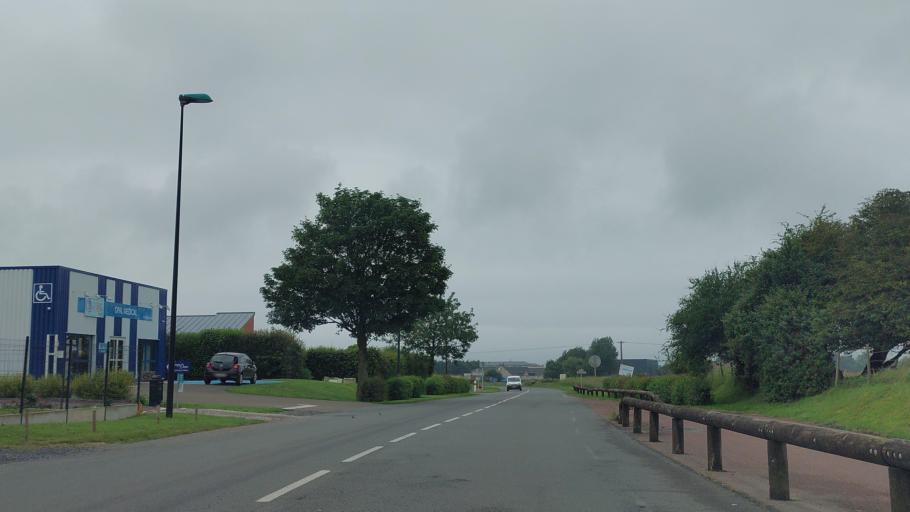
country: FR
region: Picardie
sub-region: Departement de la Somme
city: Ault
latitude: 50.0914
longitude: 1.4701
